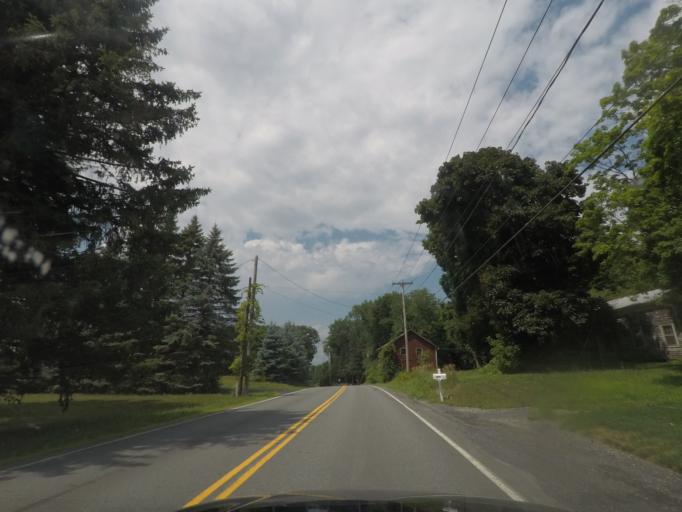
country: US
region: New York
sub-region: Rensselaer County
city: Hampton Manor
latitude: 42.6445
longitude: -73.6833
